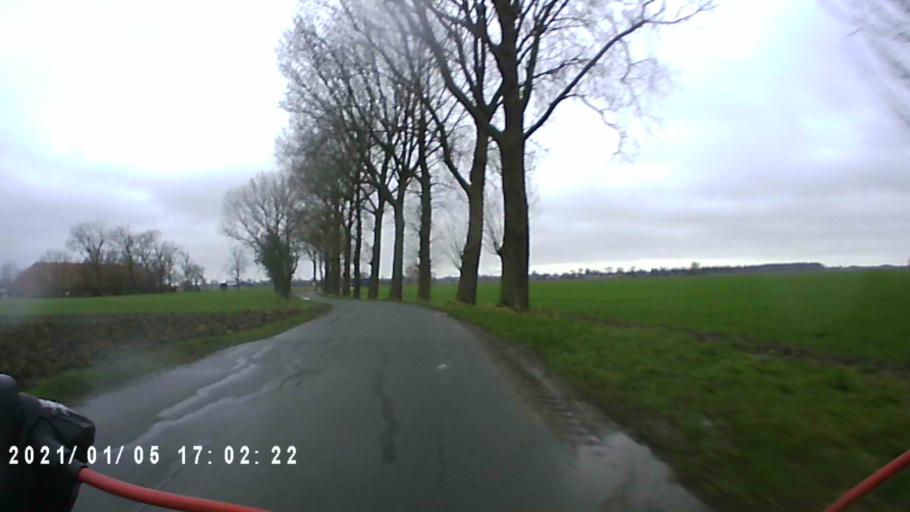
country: NL
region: Groningen
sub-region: Gemeente  Oldambt
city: Winschoten
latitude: 53.2589
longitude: 7.0419
